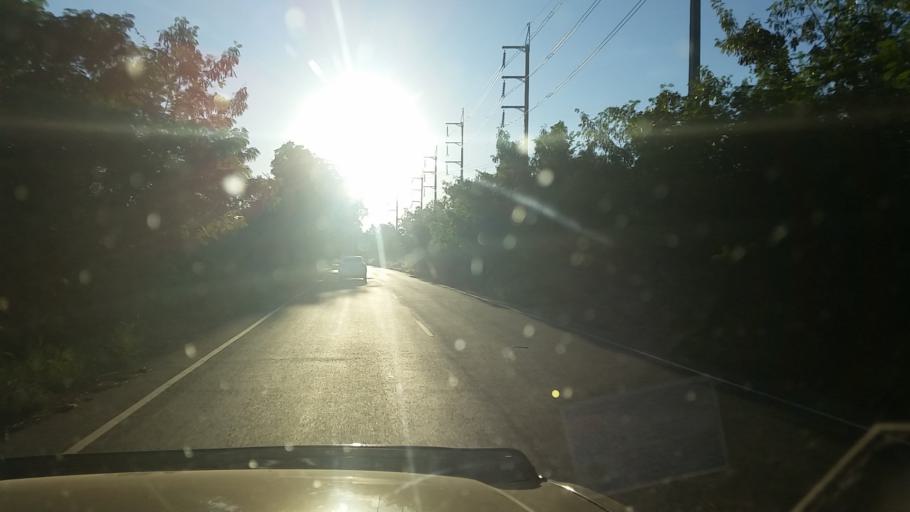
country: TH
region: Chaiyaphum
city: Sap Yai
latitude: 15.6764
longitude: 101.6779
